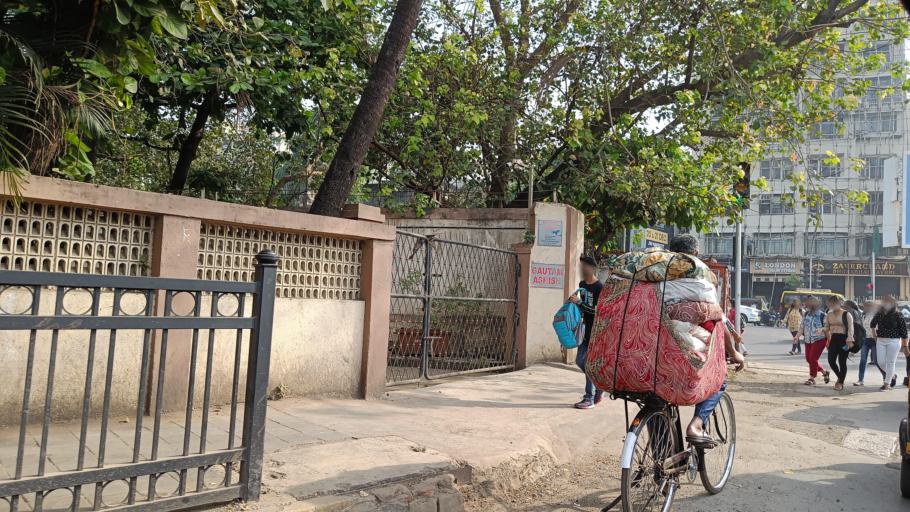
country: IN
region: Maharashtra
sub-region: Mumbai Suburban
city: Mumbai
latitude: 19.1017
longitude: 72.8391
